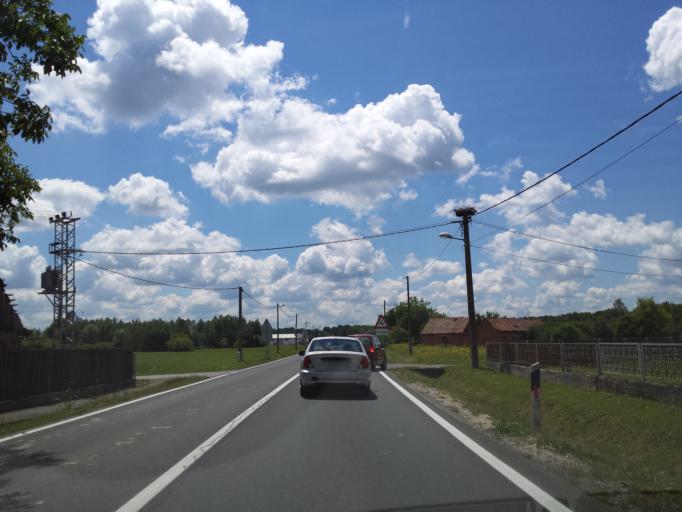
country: HR
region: Sisacko-Moslavacka
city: Lekenik
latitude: 45.5329
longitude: 16.2405
